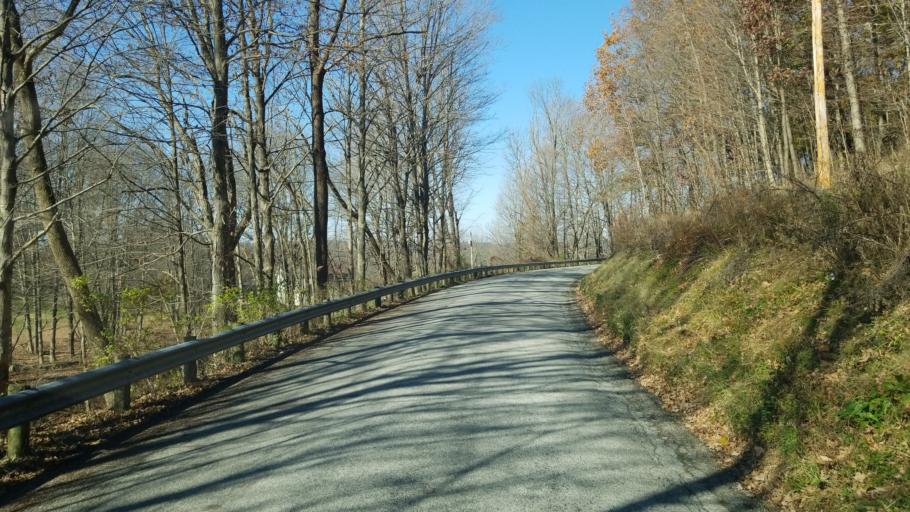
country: US
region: Ohio
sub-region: Licking County
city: Newark
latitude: 40.1468
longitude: -82.4114
